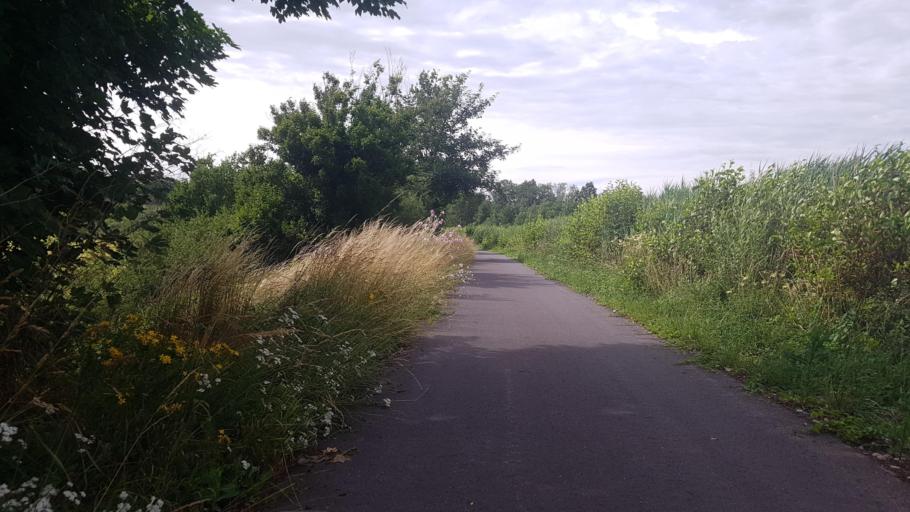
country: FR
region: Lorraine
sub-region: Departement de la Moselle
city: Dieuze
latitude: 48.6895
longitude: 6.7618
